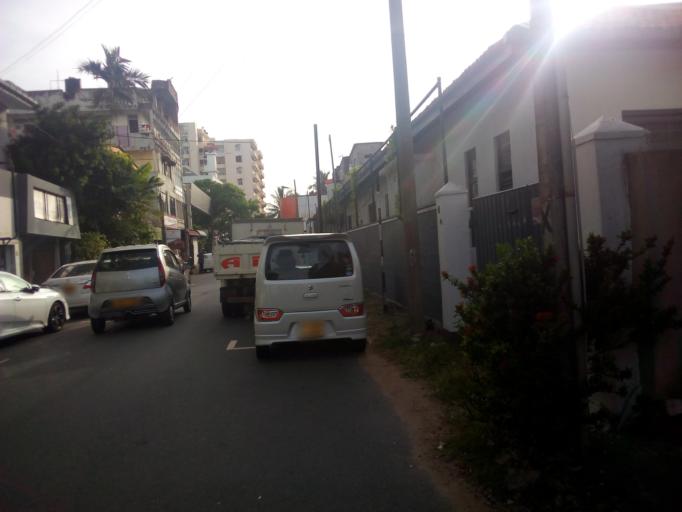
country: LK
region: Western
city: Pita Kotte
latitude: 6.8892
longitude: 79.8578
